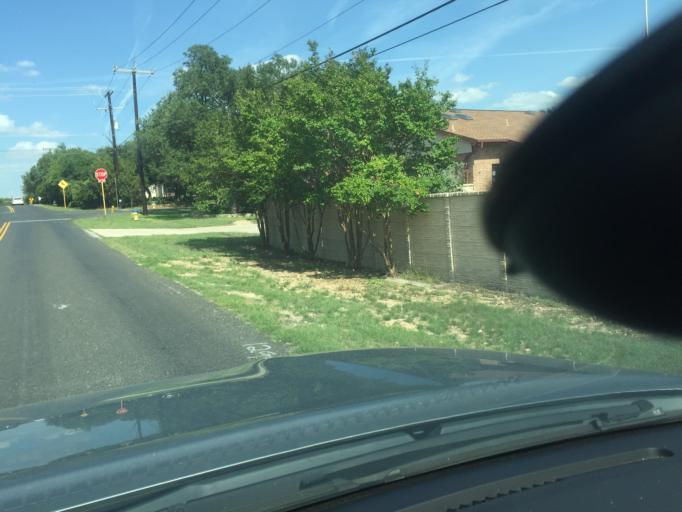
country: US
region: Texas
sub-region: Bexar County
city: Timberwood Park
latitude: 29.6850
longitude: -98.4861
